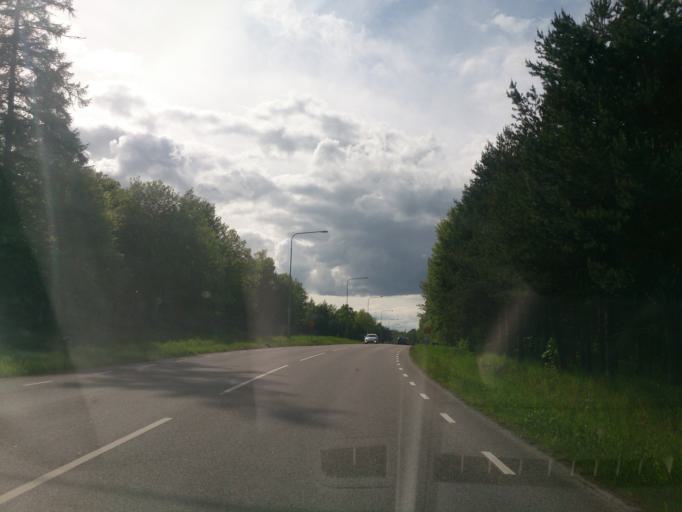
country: SE
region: OEstergoetland
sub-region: Linkopings Kommun
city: Malmslatt
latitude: 58.4101
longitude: 15.5380
